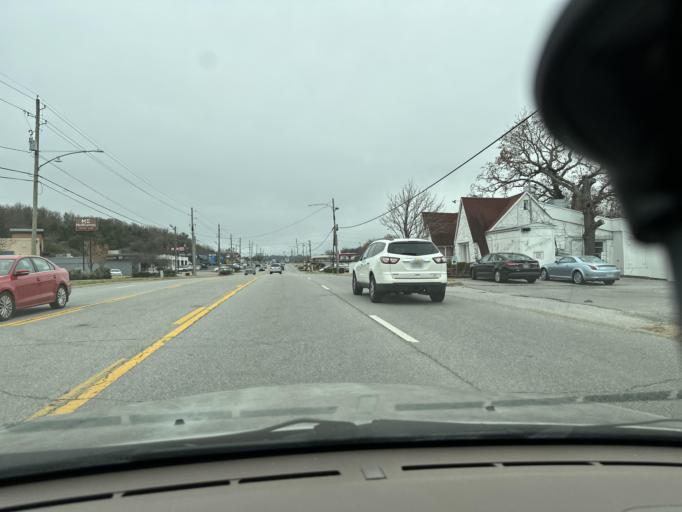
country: US
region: Arkansas
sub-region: Washington County
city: Johnson
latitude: 36.1046
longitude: -94.1474
